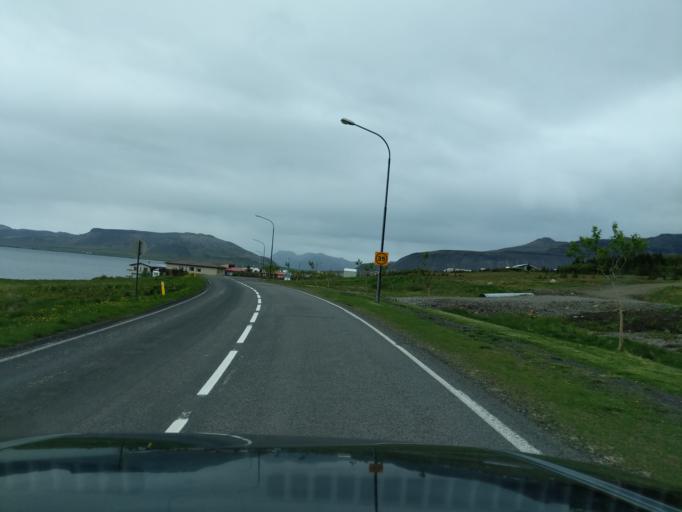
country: IS
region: West
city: Olafsvik
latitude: 64.9223
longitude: -23.2774
